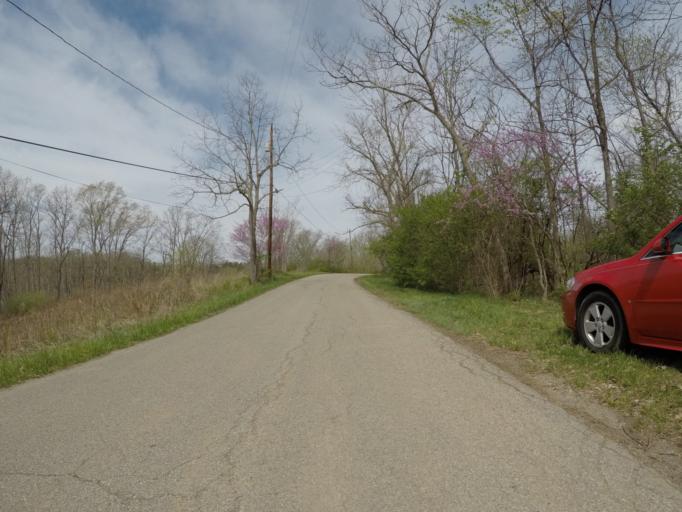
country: US
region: West Virginia
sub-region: Wayne County
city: Lavalette
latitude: 38.3460
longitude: -82.3891
